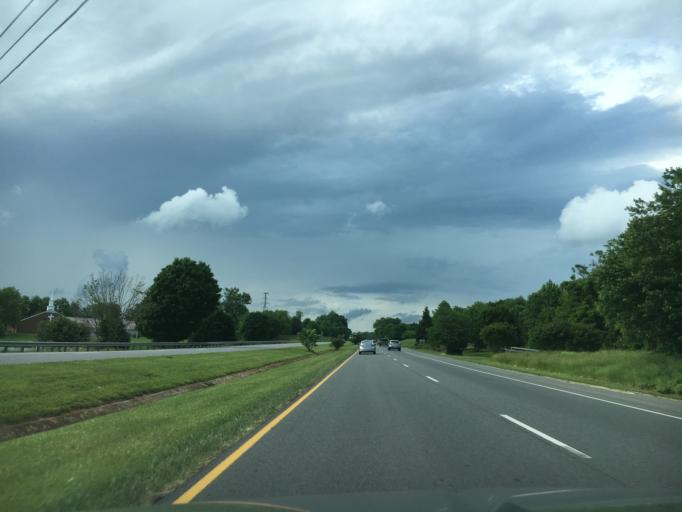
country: US
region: Virginia
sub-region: City of Lynchburg
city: West Lynchburg
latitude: 37.3843
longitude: -79.2227
